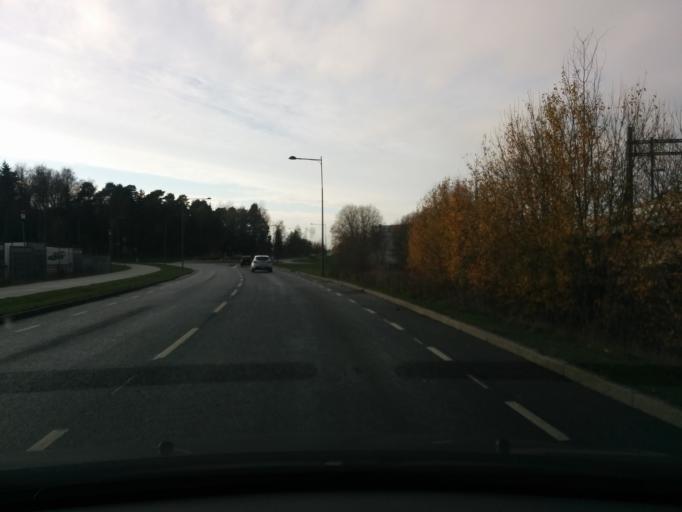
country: SE
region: Stockholm
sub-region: Jarfalla Kommun
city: Jakobsberg
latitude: 59.3875
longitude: 17.8824
